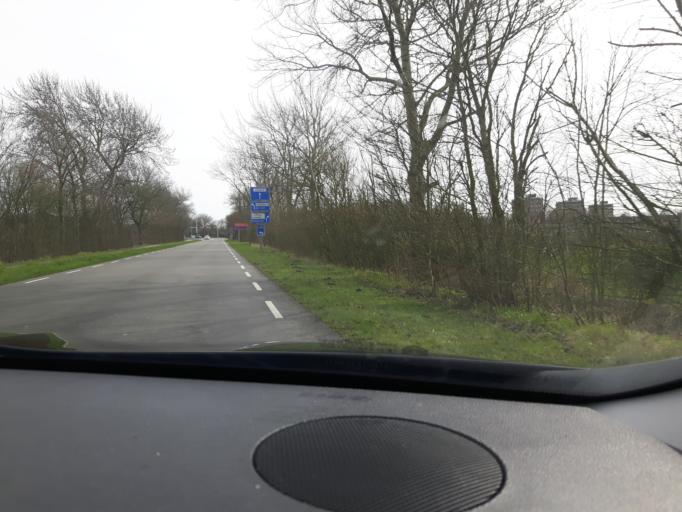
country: NL
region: Zeeland
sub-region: Gemeente Middelburg
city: Middelburg
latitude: 51.5092
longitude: 3.6004
